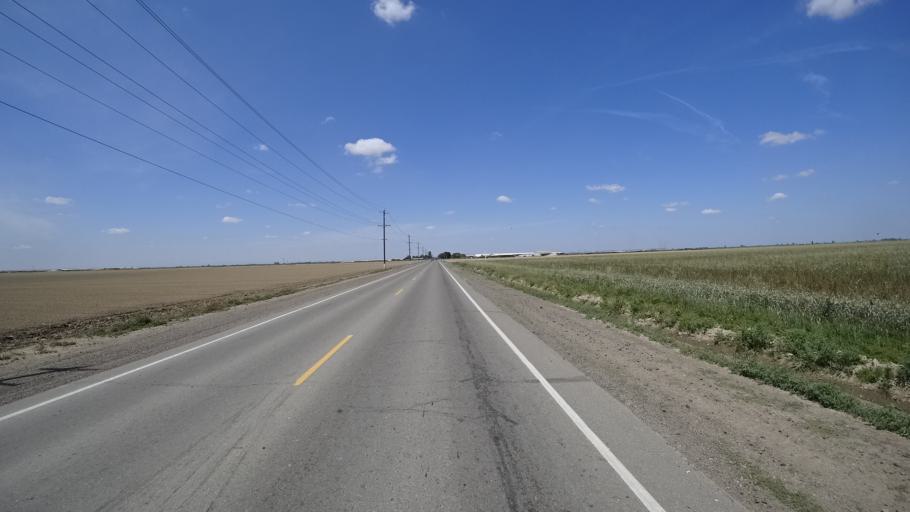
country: US
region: California
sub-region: Tulare County
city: Goshen
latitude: 36.2983
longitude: -119.5135
